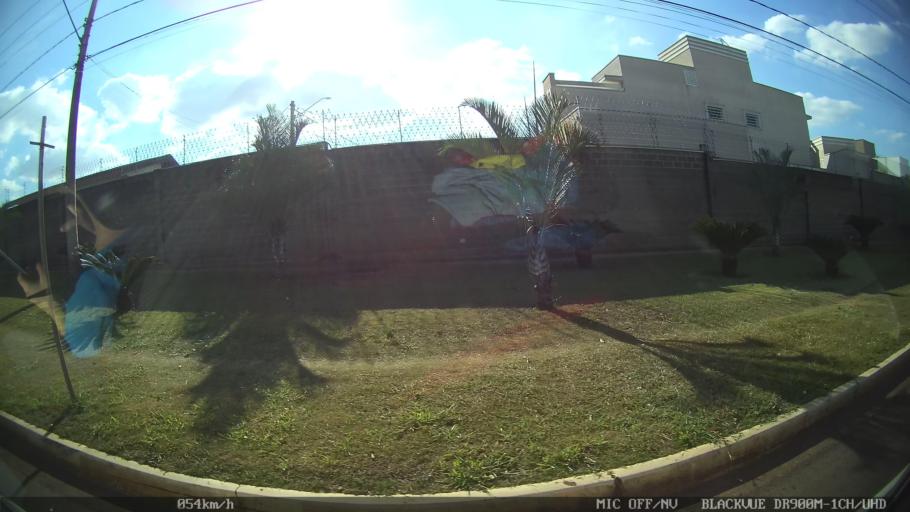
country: BR
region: Sao Paulo
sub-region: Nova Odessa
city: Nova Odessa
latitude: -22.7931
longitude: -47.3121
